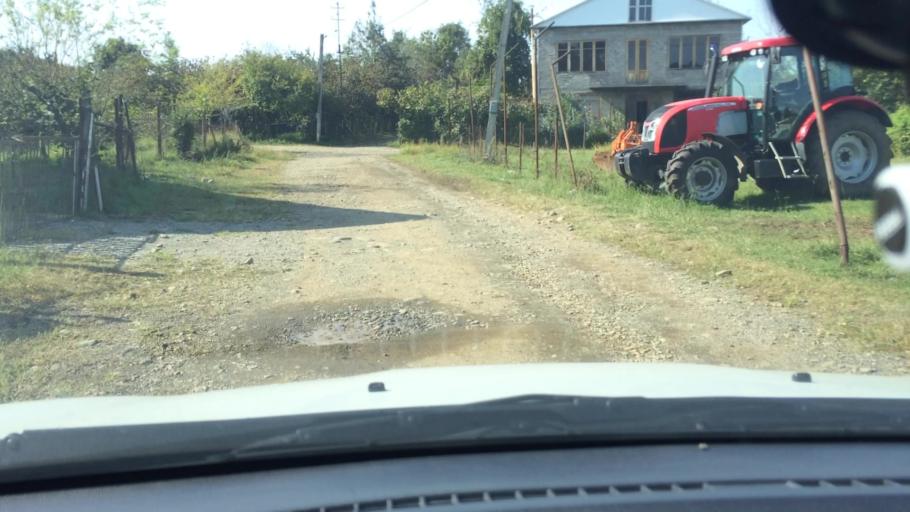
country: GE
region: Ajaria
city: Kobuleti
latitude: 41.8093
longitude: 41.8182
